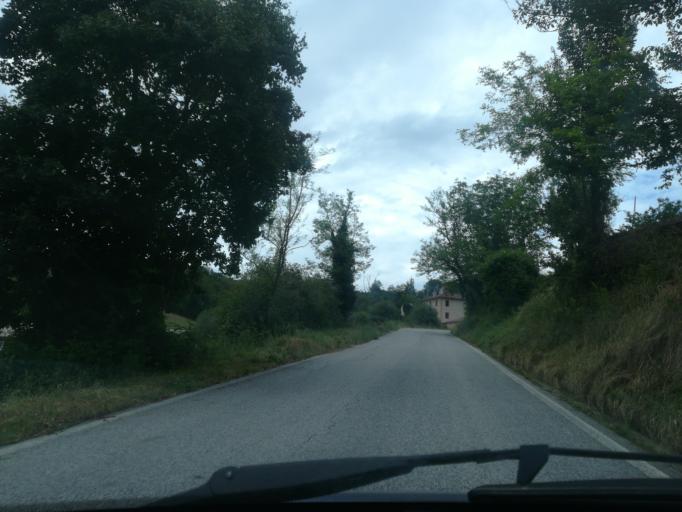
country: IT
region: The Marches
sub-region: Province of Fermo
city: Montefortino
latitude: 42.9358
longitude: 13.3743
